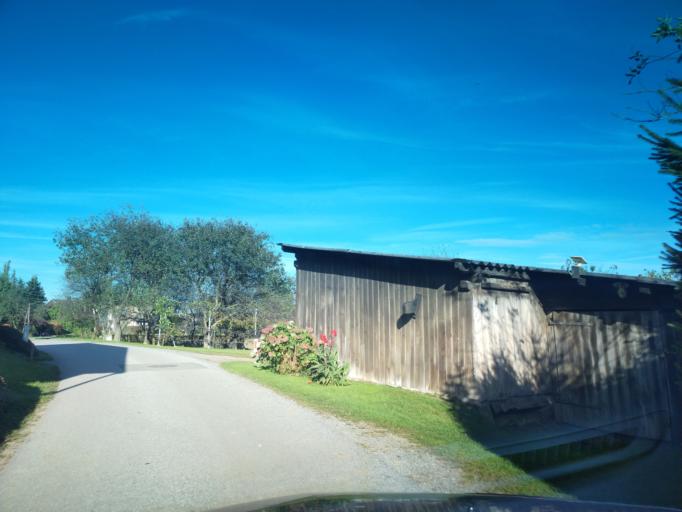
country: AT
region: Styria
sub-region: Politischer Bezirk Deutschlandsberg
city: Sankt Martin im Sulmtal
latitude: 46.7322
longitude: 15.3112
